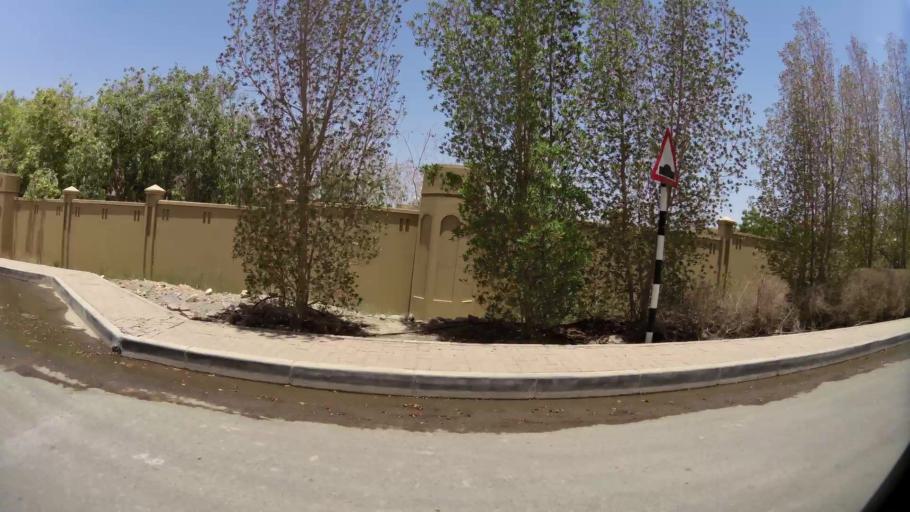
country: OM
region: Muhafazat Masqat
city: Bawshar
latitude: 23.6041
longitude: 58.4777
